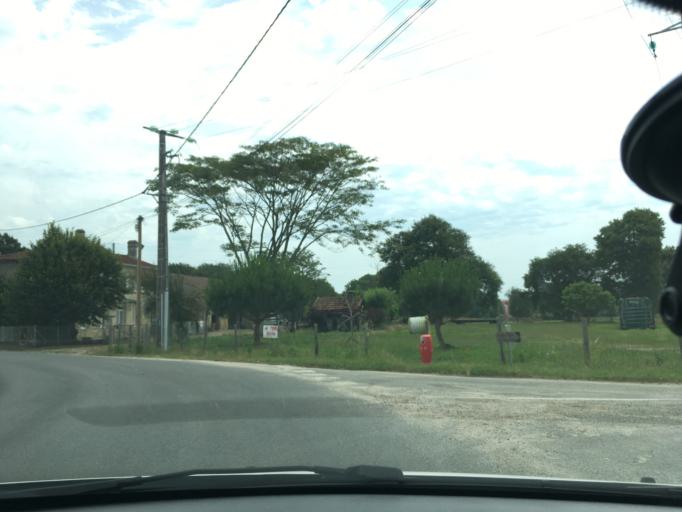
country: FR
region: Aquitaine
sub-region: Departement de la Gironde
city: Gaillan-en-Medoc
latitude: 45.3364
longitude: -0.9936
